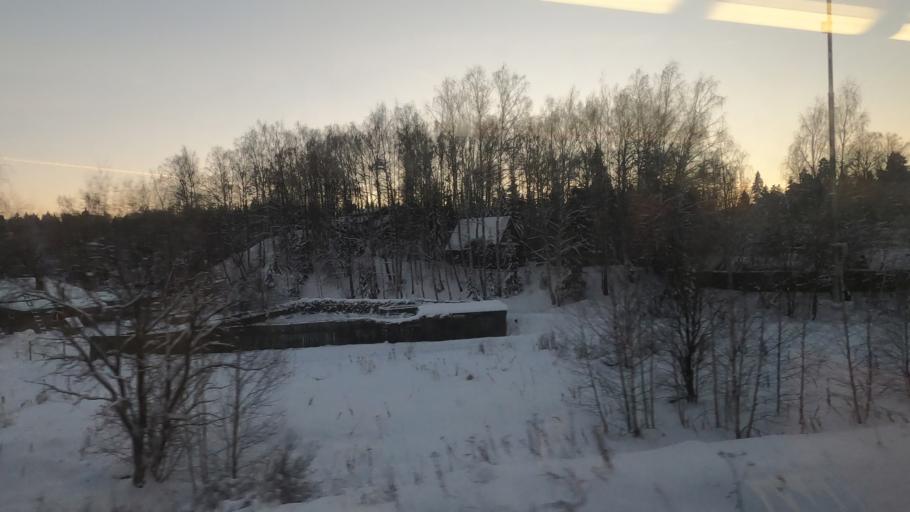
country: RU
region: Moskovskaya
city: Yermolino
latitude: 56.1365
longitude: 37.5123
